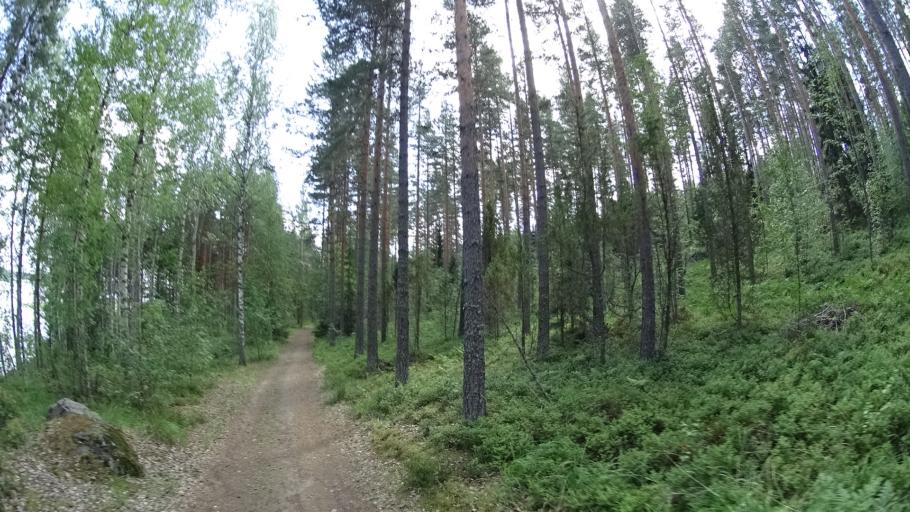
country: FI
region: Haeme
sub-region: Forssa
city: Tammela
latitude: 60.7754
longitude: 23.8582
